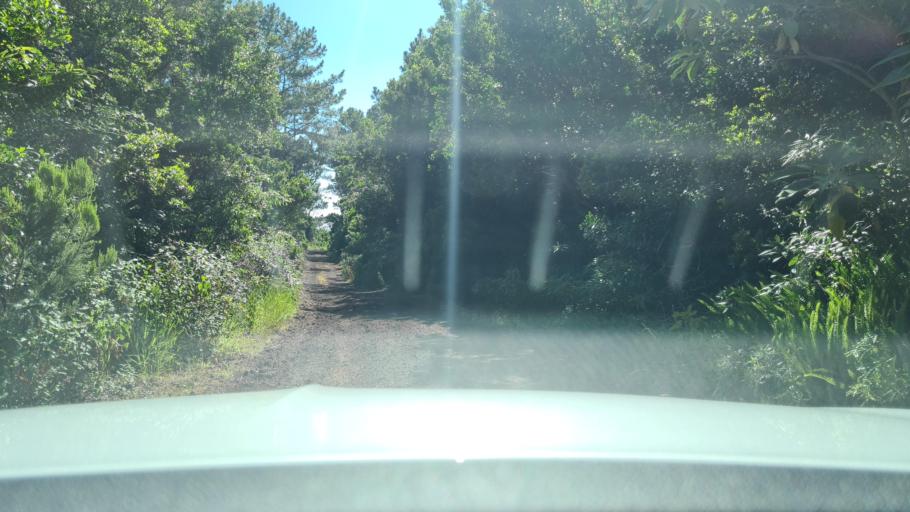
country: PT
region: Azores
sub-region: Sao Roque do Pico
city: Sao Roque do Pico
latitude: 38.4126
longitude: -28.3163
